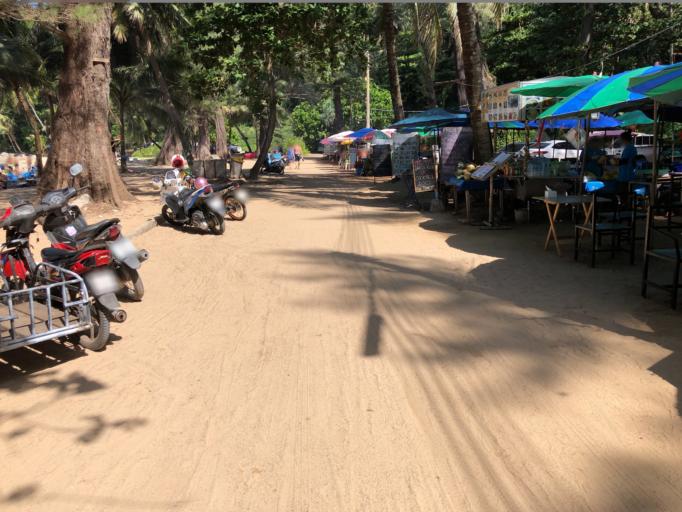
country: TH
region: Phuket
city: Thalang
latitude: 7.9782
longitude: 98.2784
